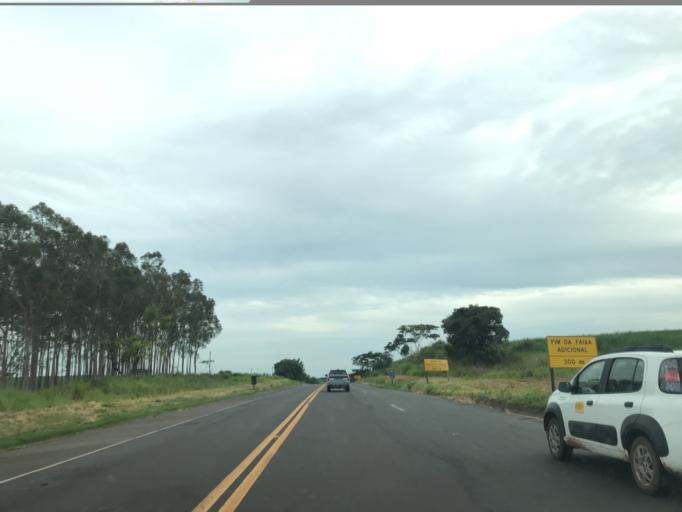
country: BR
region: Sao Paulo
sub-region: Tupa
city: Tupa
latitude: -21.6049
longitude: -50.4711
